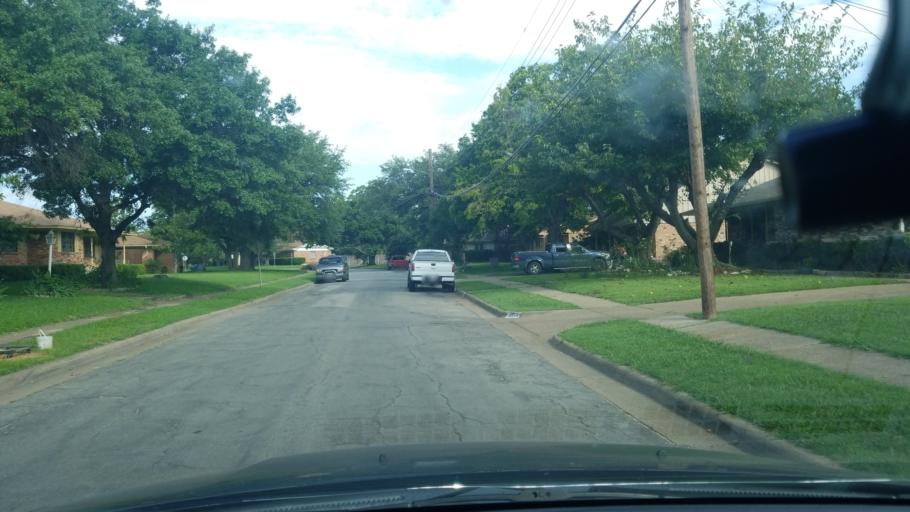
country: US
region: Texas
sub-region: Dallas County
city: Balch Springs
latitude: 32.7511
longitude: -96.6637
